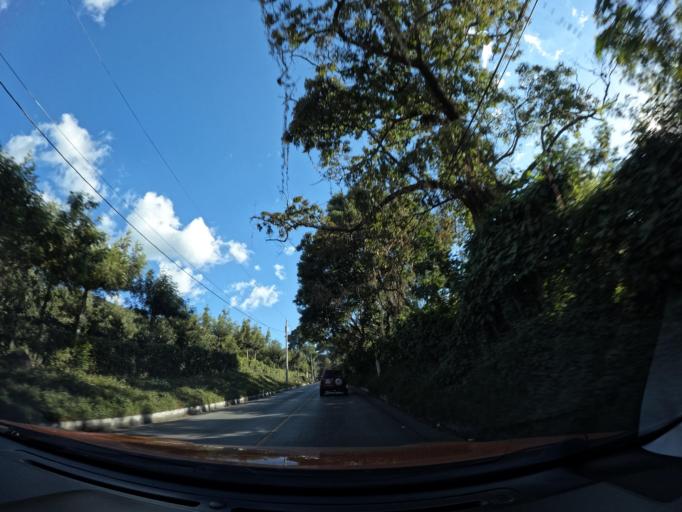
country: GT
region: Sacatepequez
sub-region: Municipio de Santa Maria de Jesus
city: Santa Maria de Jesus
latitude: 14.5295
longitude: -90.7272
